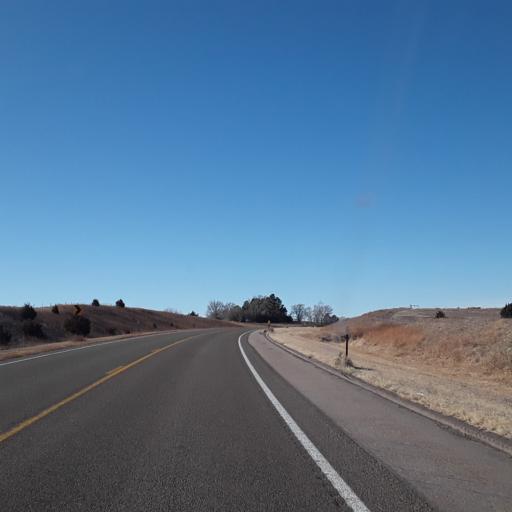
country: US
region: Nebraska
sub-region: Frontier County
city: Stockville
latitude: 40.6318
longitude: -100.5828
